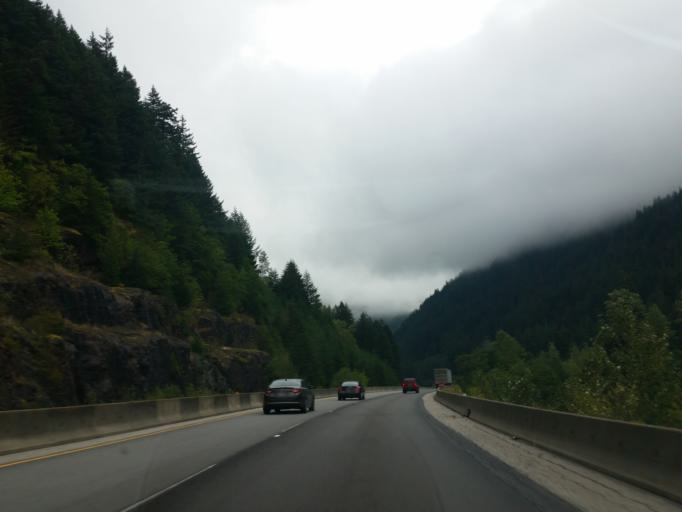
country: CA
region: British Columbia
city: Hope
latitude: 49.4398
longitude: -121.2977
